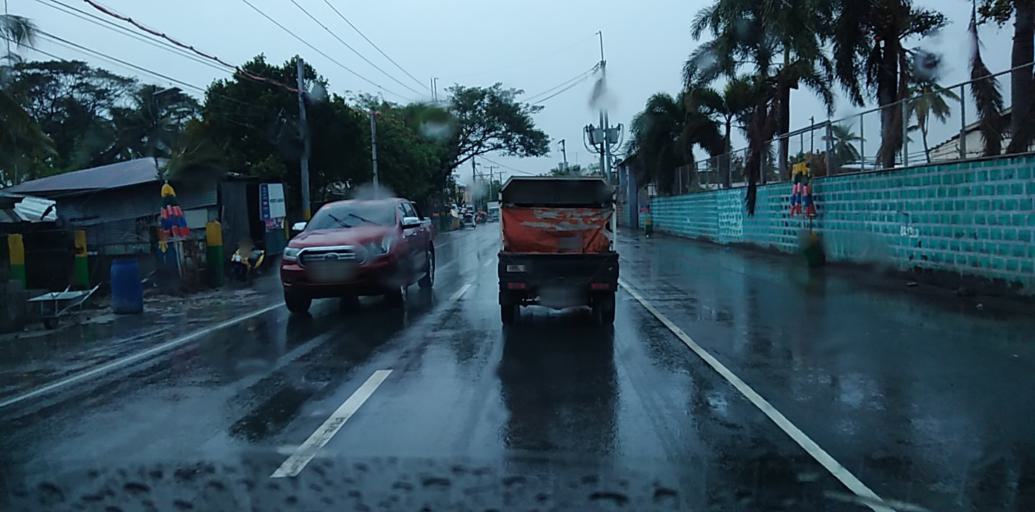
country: PH
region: Central Luzon
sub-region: Province of Bulacan
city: Bulualto
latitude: 15.2089
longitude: 120.9560
